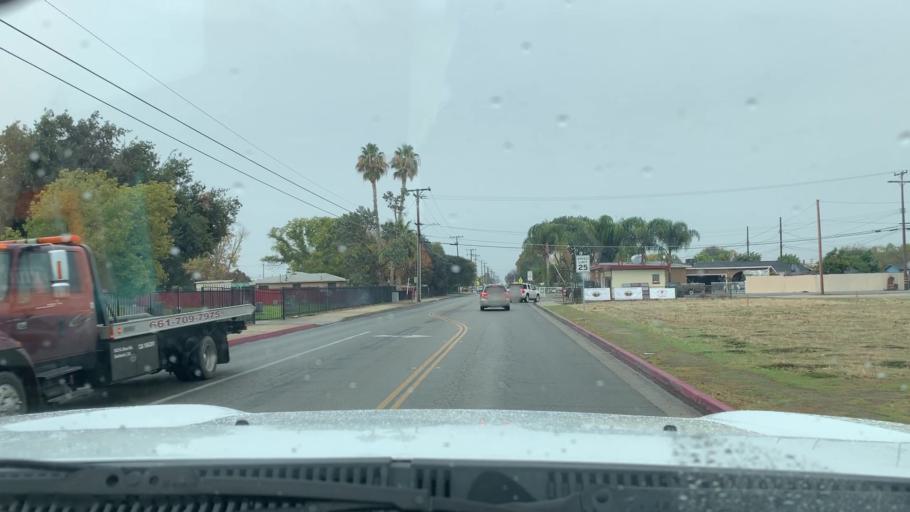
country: US
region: California
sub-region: Kern County
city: Delano
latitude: 35.7614
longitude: -119.2583
